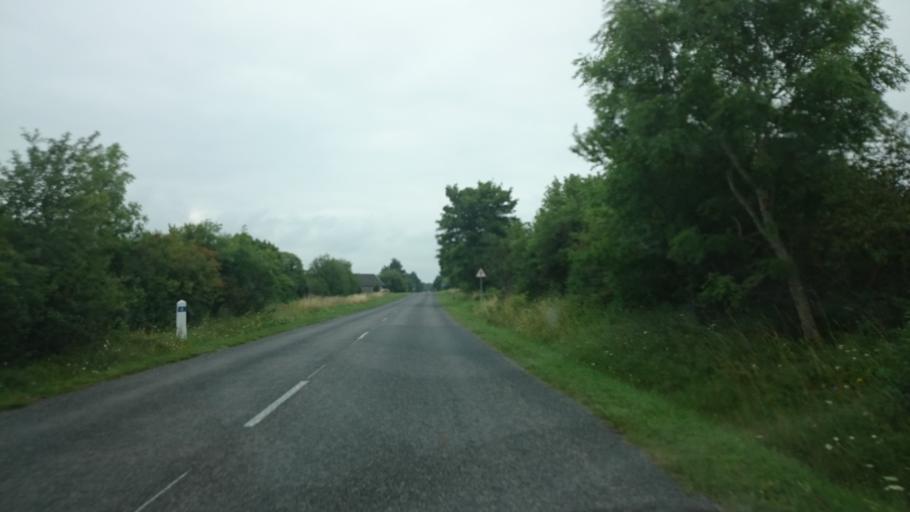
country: EE
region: Saare
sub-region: Orissaare vald
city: Orissaare
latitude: 58.5831
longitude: 23.0265
